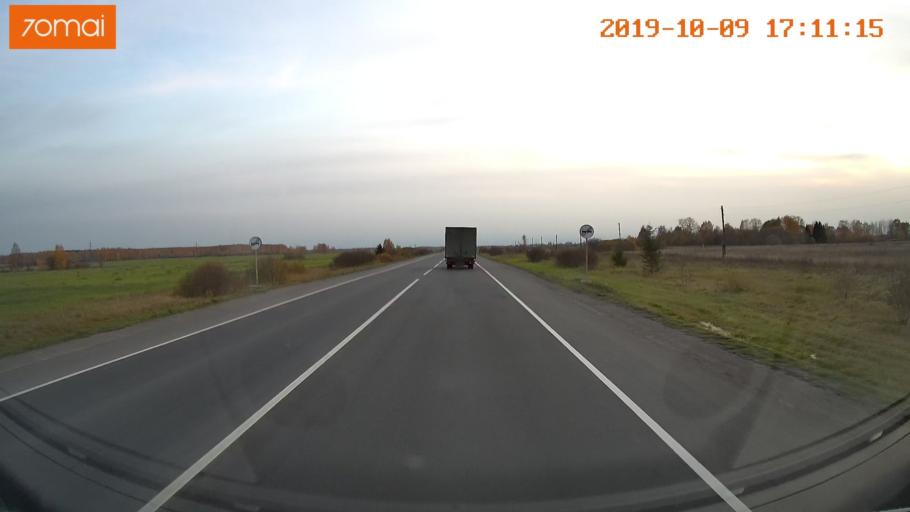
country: RU
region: Ivanovo
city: Privolzhsk
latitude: 57.3453
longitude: 41.2513
